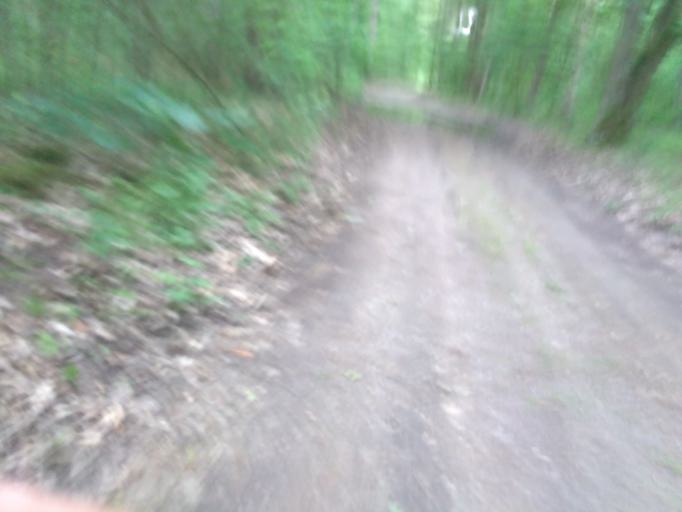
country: DE
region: Brandenburg
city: Hohenleipisch
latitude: 51.5026
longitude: 13.5275
